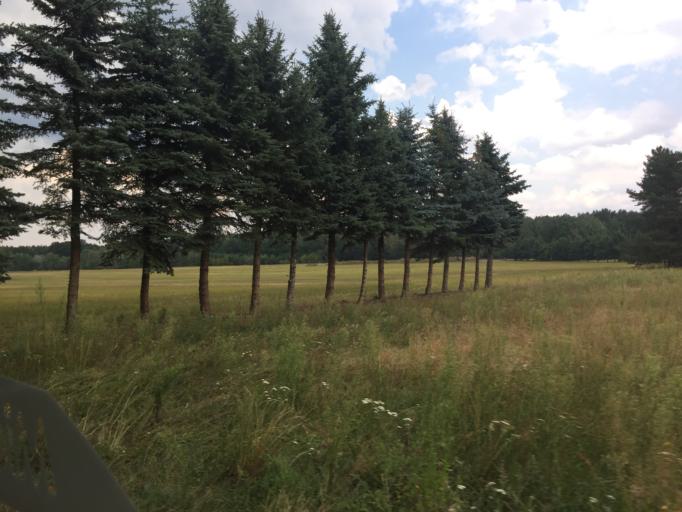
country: DE
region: Saxony
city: Trebendorf
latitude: 51.5188
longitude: 14.5577
